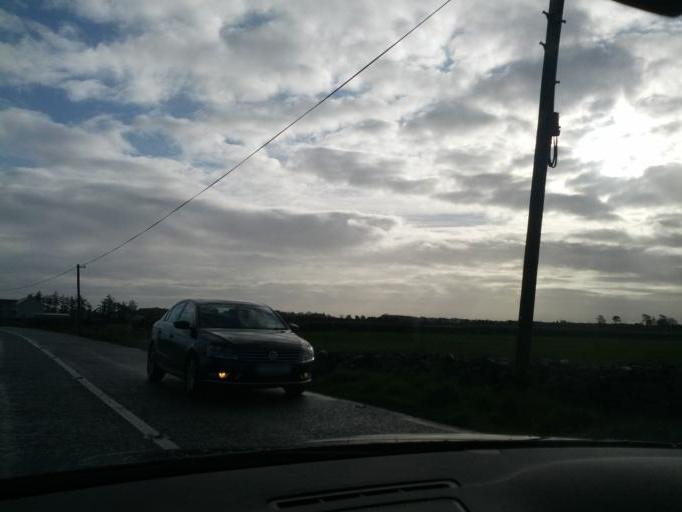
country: IE
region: Connaught
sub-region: County Galway
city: Athenry
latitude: 53.3308
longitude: -8.8218
